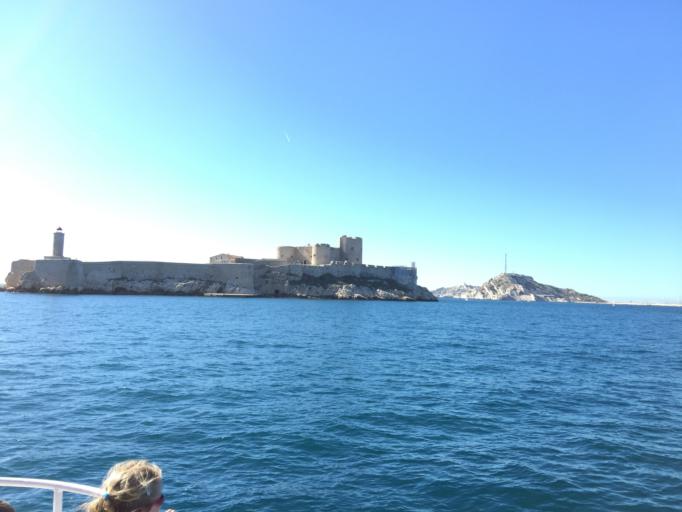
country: FR
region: Provence-Alpes-Cote d'Azur
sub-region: Departement des Bouches-du-Rhone
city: Marseille 07
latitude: 43.2826
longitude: 5.3287
